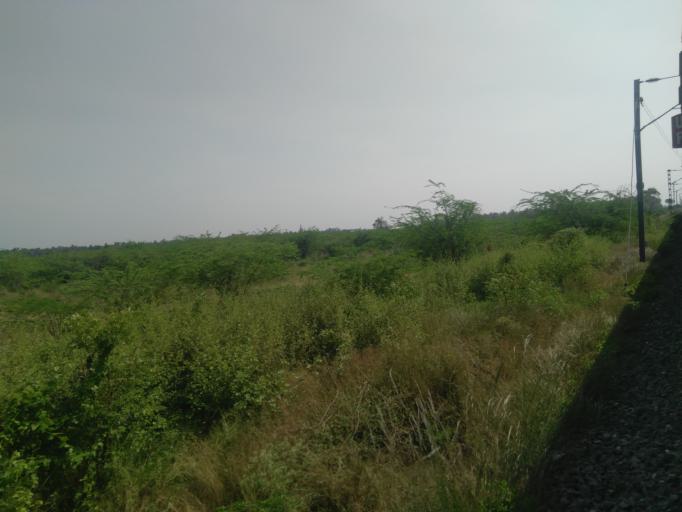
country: IN
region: Tamil Nadu
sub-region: Coimbatore
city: Periyanayakkanpalaiyam
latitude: 11.1391
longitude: 76.9487
